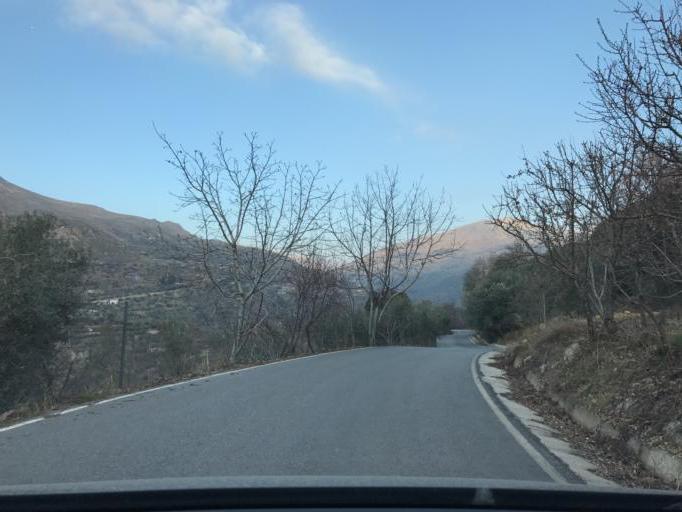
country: ES
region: Andalusia
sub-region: Provincia de Granada
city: Guejar-Sierra
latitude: 37.1508
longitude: -3.4353
